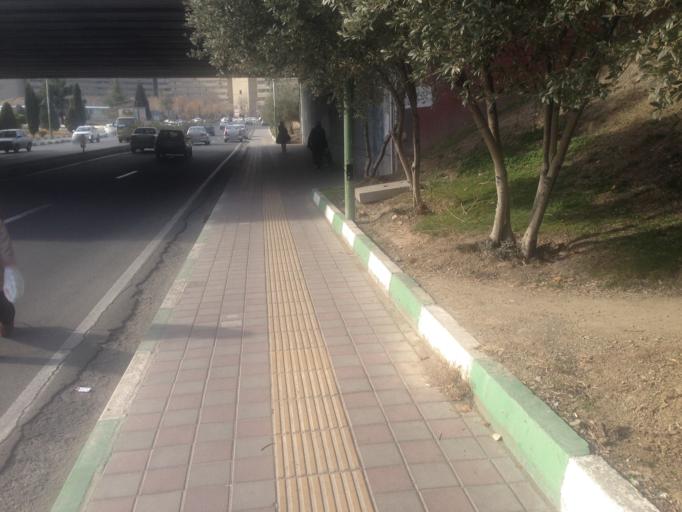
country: IR
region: Tehran
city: Tehran
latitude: 35.7126
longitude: 51.3089
